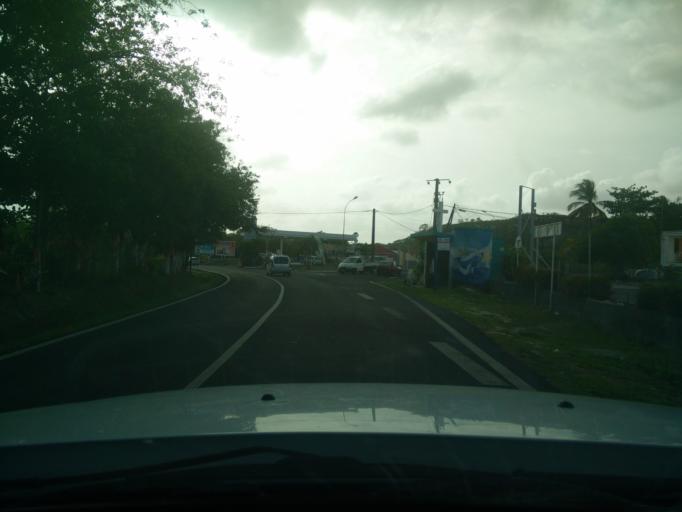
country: GP
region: Guadeloupe
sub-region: Guadeloupe
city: Saint-Francois
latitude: 16.2598
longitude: -61.2920
